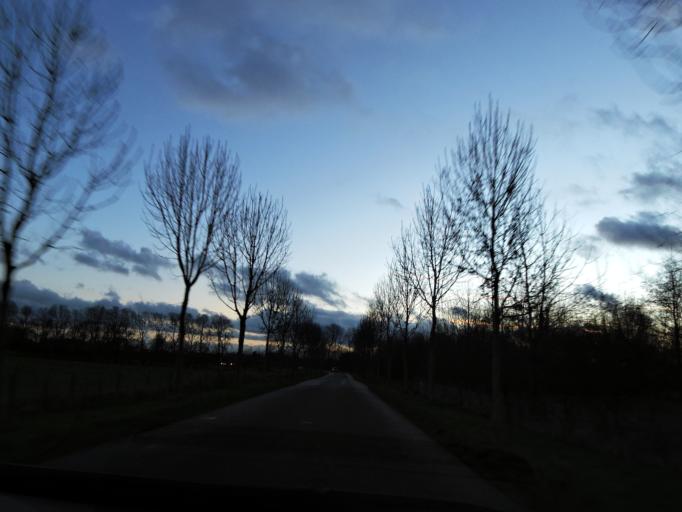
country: NL
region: Limburg
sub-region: Gemeente Roermond
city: Leeuwen
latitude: 51.2186
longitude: 6.0058
